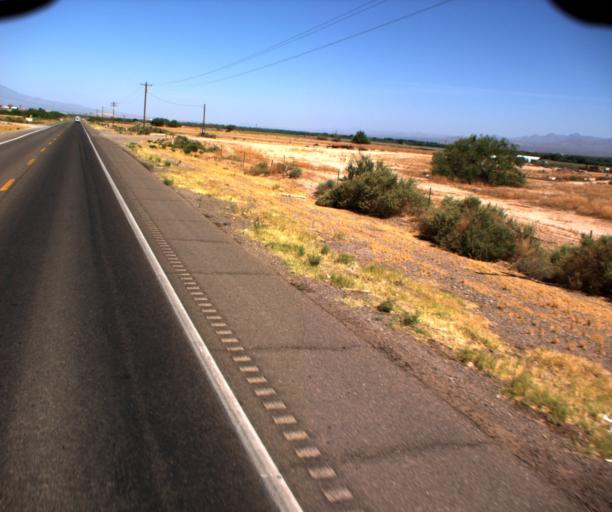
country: US
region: Arizona
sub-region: Graham County
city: Pima
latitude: 32.9217
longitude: -109.8715
